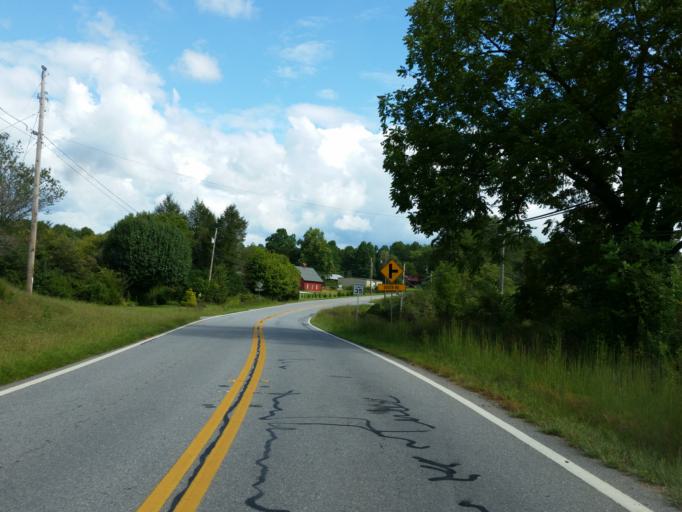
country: US
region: Georgia
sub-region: Fannin County
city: Blue Ridge
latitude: 34.8732
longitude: -84.2410
